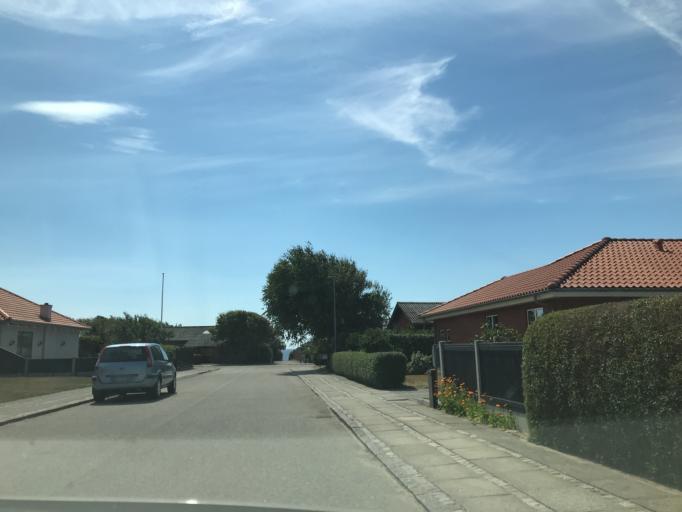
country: DK
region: Central Jutland
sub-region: Ringkobing-Skjern Kommune
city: Ringkobing
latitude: 56.0829
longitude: 8.2540
